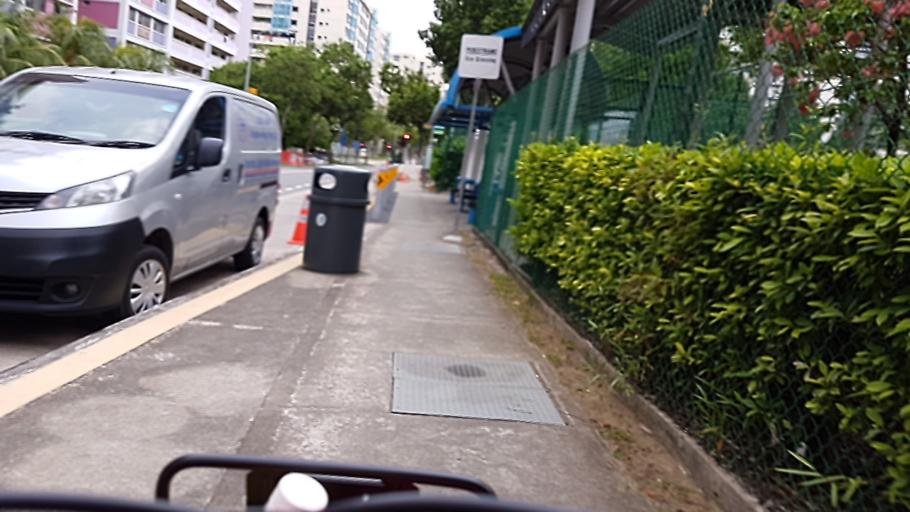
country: MY
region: Johor
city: Kampung Pasir Gudang Baru
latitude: 1.3735
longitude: 103.9596
